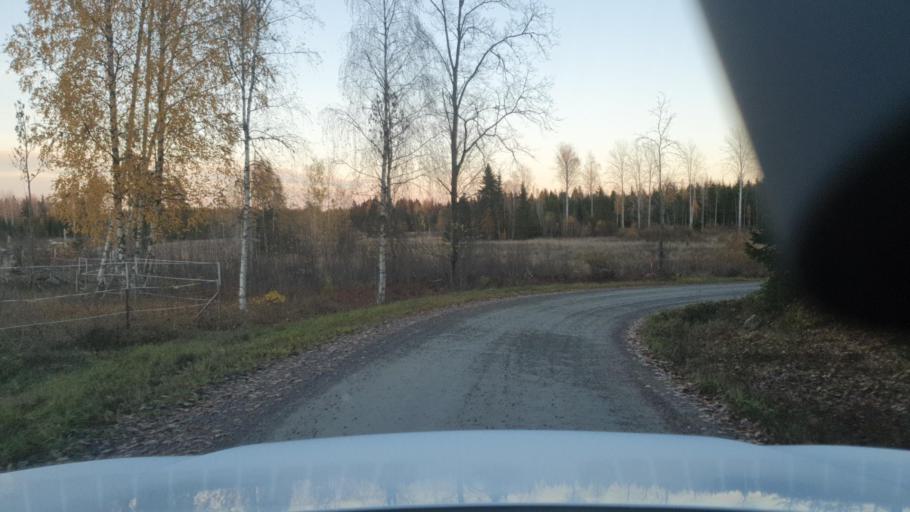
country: SE
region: Uppsala
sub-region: Alvkarleby Kommun
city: AElvkarleby
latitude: 60.4841
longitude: 17.4938
